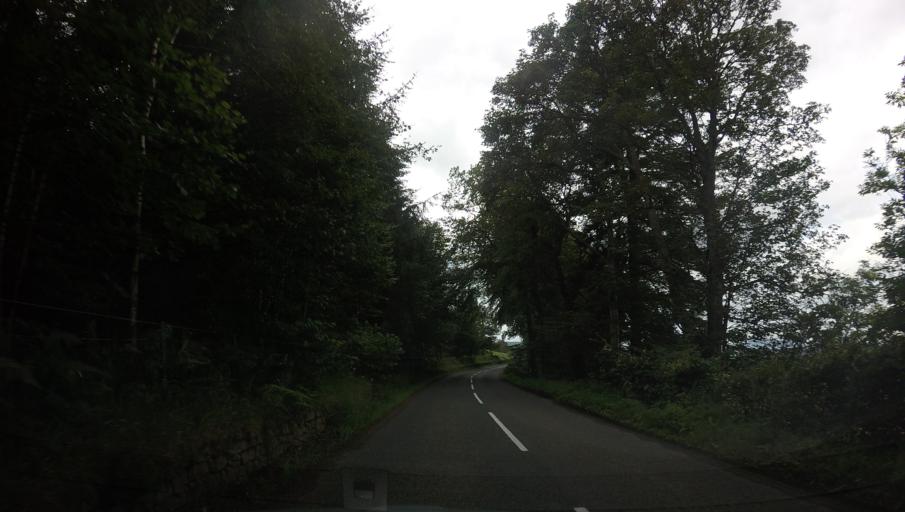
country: GB
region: Scotland
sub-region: Aberdeenshire
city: Aboyne
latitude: 57.0618
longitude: -2.6971
